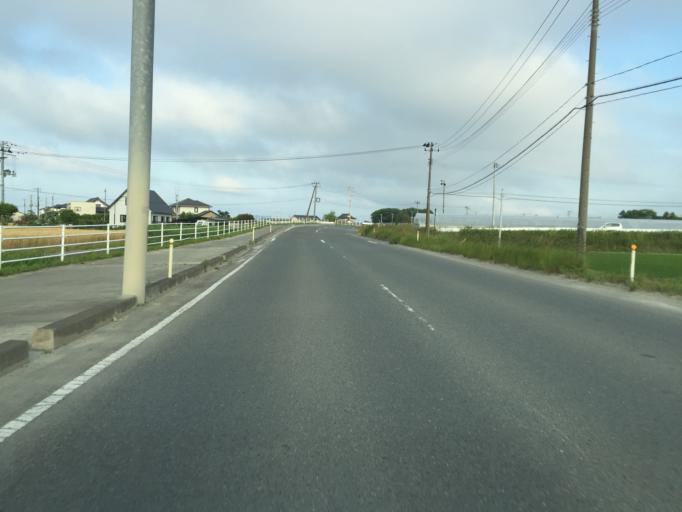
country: JP
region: Miyagi
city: Marumori
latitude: 37.7848
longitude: 140.9611
